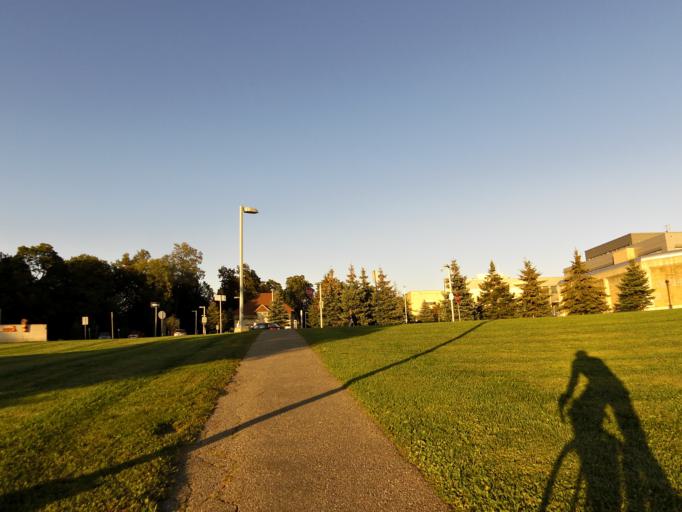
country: CA
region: Ontario
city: Ottawa
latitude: 45.3894
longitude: -75.7319
